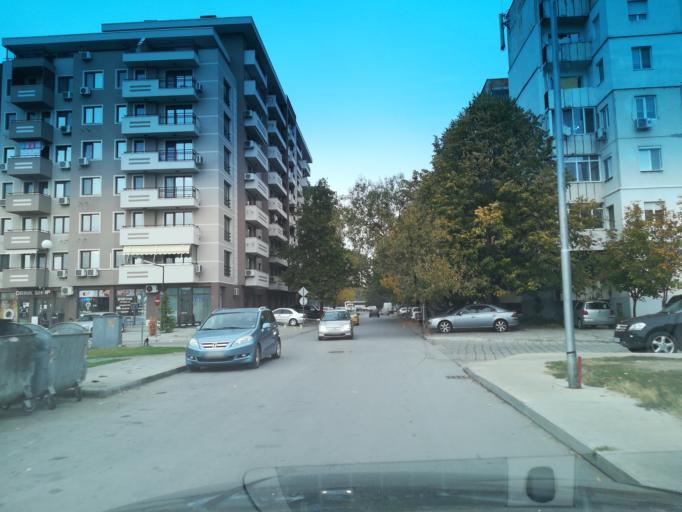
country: BG
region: Plovdiv
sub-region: Obshtina Plovdiv
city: Plovdiv
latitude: 42.1370
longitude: 24.7932
